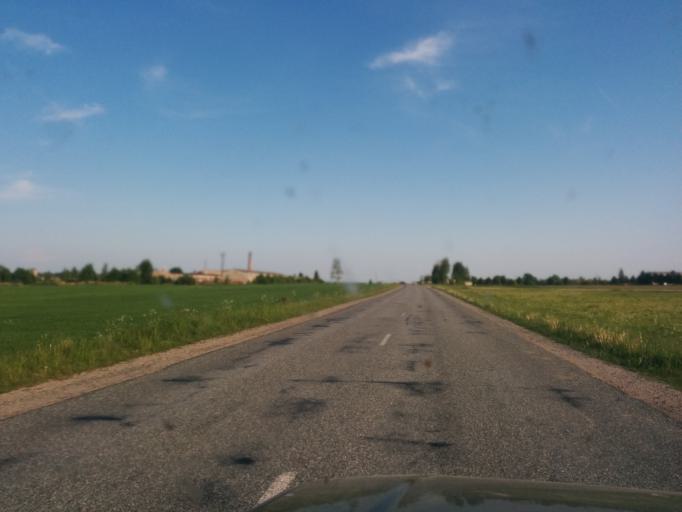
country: LV
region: Talsu Rajons
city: Valdemarpils
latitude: 57.3505
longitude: 22.4974
